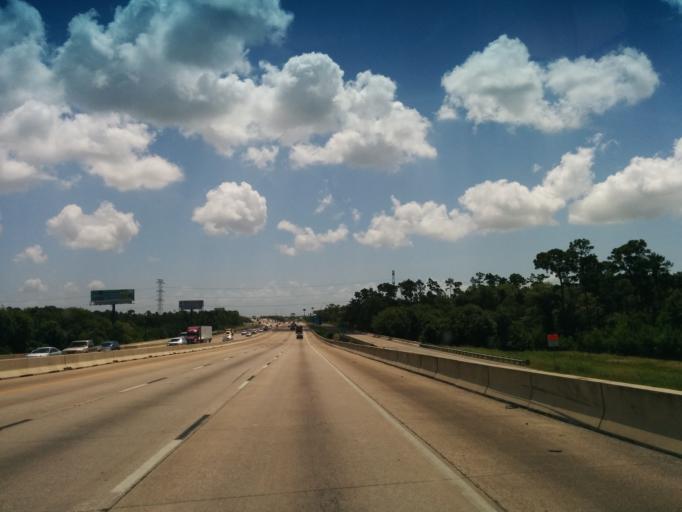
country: US
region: Texas
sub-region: Chambers County
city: Mont Belvieu
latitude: 29.8211
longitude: -94.9120
